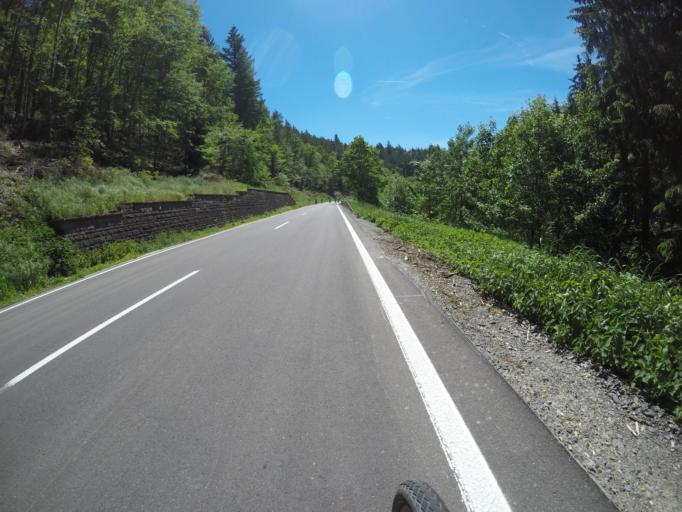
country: DE
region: Baden-Wuerttemberg
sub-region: Karlsruhe Region
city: Tiefenbronn
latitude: 48.8125
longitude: 8.8052
